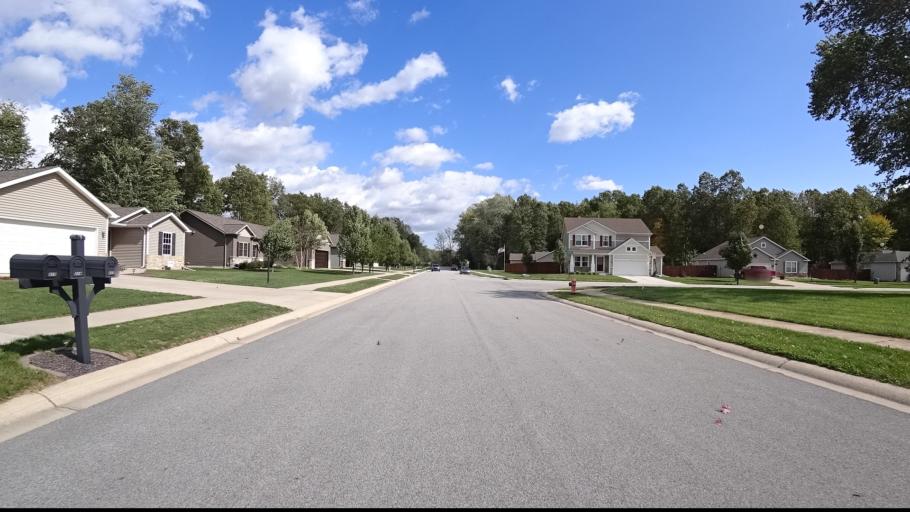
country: US
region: Indiana
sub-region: Porter County
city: Burns Harbor
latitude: 41.6005
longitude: -87.1077
